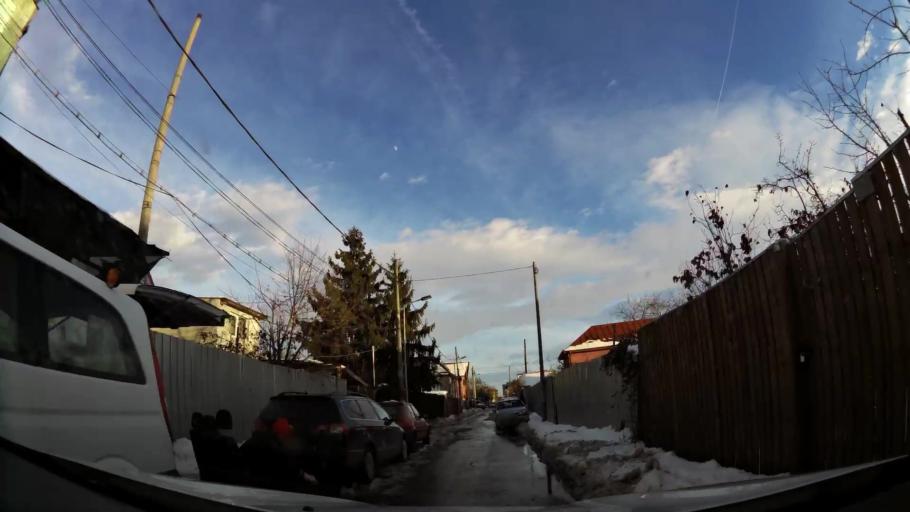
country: RO
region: Ilfov
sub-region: Comuna Popesti-Leordeni
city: Popesti-Leordeni
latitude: 44.3722
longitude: 26.1313
